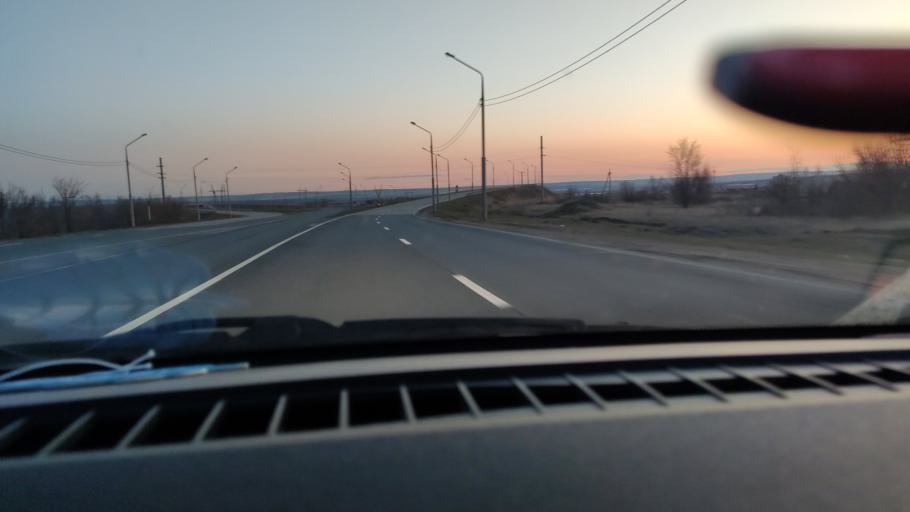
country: RU
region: Saratov
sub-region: Saratovskiy Rayon
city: Saratov
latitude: 51.6646
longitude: 45.9996
